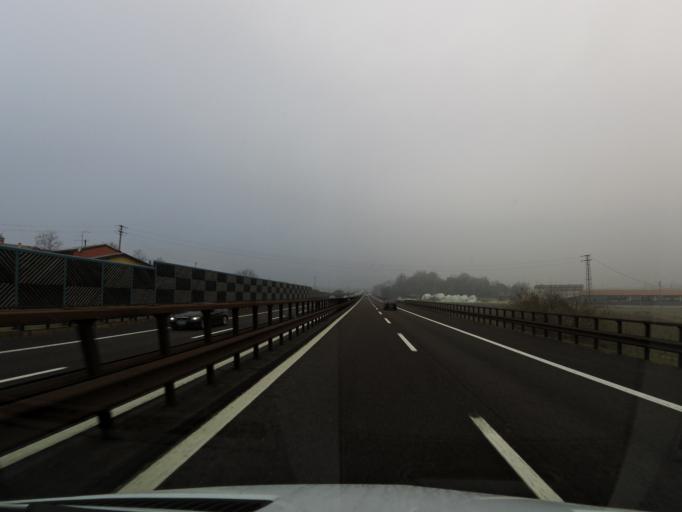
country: IT
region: Veneto
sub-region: Provincia di Verona
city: Pastrengo
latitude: 45.4903
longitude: 10.7912
